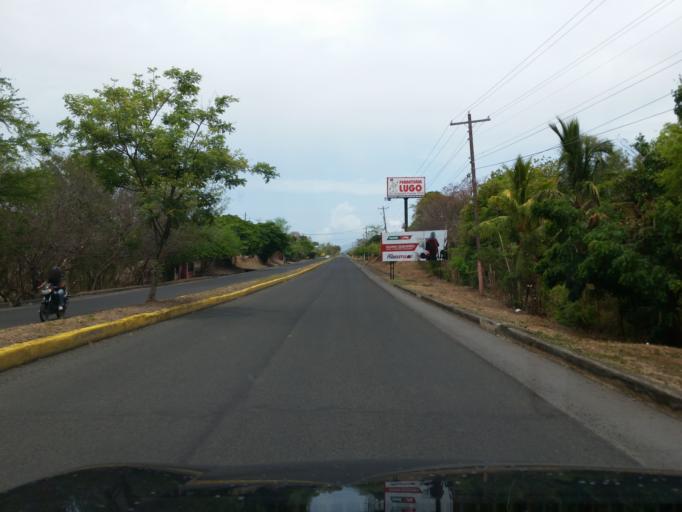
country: NI
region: Granada
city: Granada
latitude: 11.9544
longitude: -85.9886
